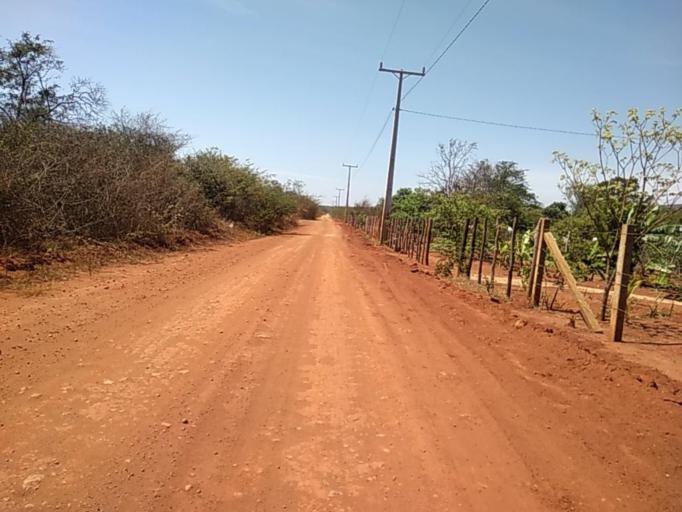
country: BR
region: Bahia
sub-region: Caetite
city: Caetite
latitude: -13.9896
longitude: -42.5081
